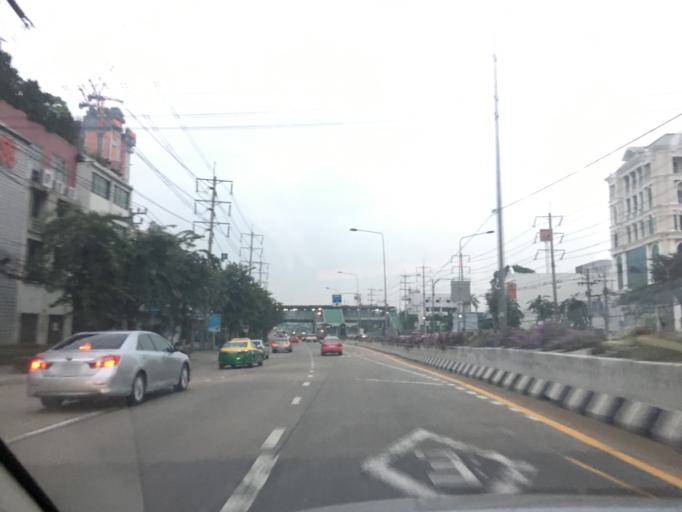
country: TH
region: Bangkok
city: Rat Burana
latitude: 13.6875
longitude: 100.5172
